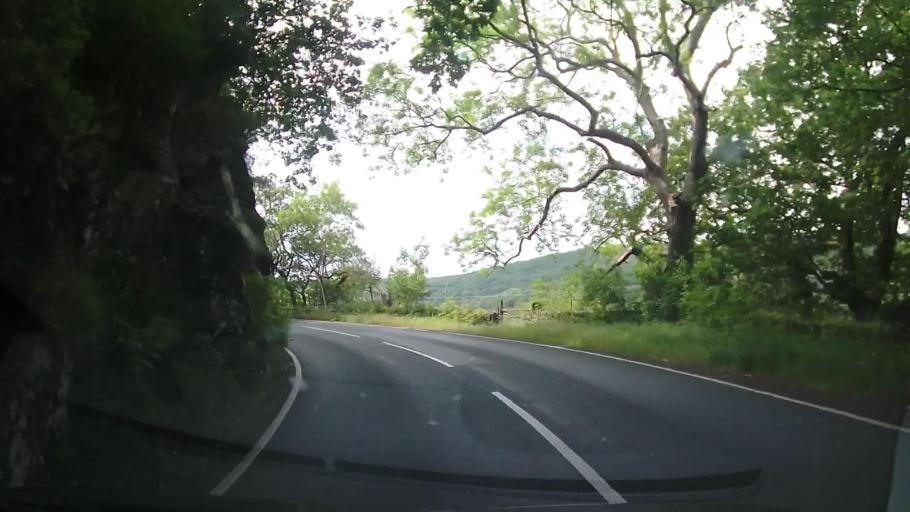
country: GB
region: Wales
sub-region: Gwynedd
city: Maentwrog
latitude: 52.9366
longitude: -4.0217
